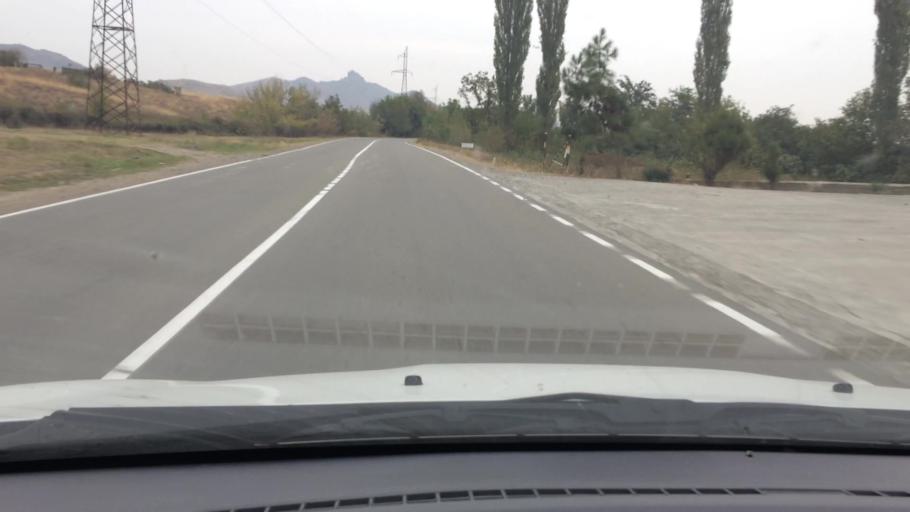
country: GE
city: Naghvarevi
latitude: 41.3281
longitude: 44.8023
